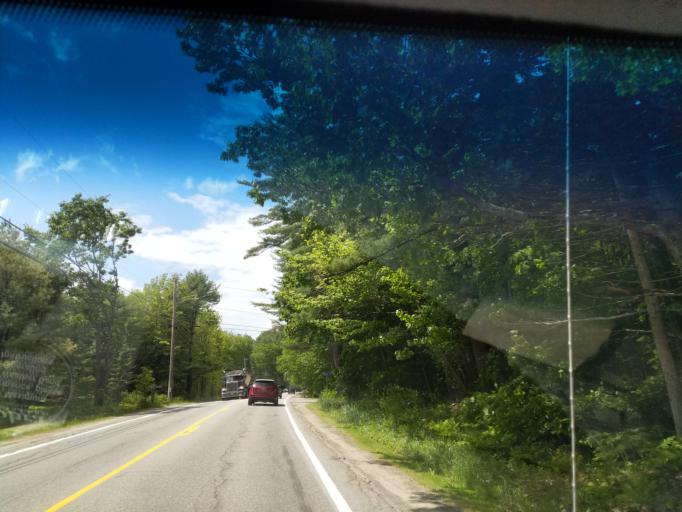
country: US
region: Maine
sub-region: Cumberland County
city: Westbrook
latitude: 43.6269
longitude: -70.3731
